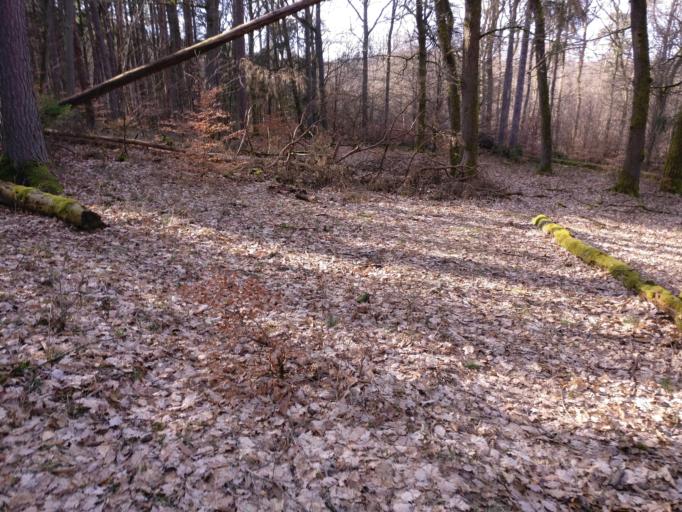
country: DE
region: Hesse
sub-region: Regierungsbezirk Giessen
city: Greifenstein
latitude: 50.6294
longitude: 8.2853
